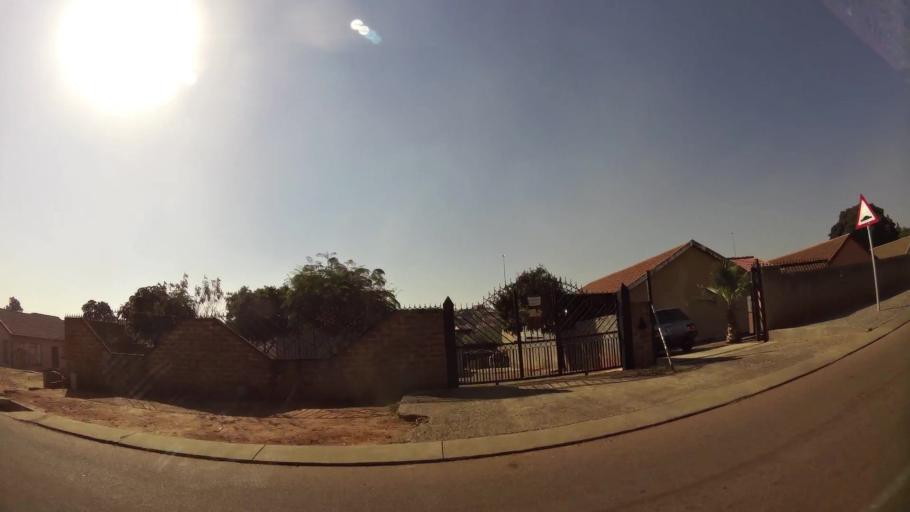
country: ZA
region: Gauteng
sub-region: City of Tshwane Metropolitan Municipality
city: Mabopane
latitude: -25.5375
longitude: 28.0905
